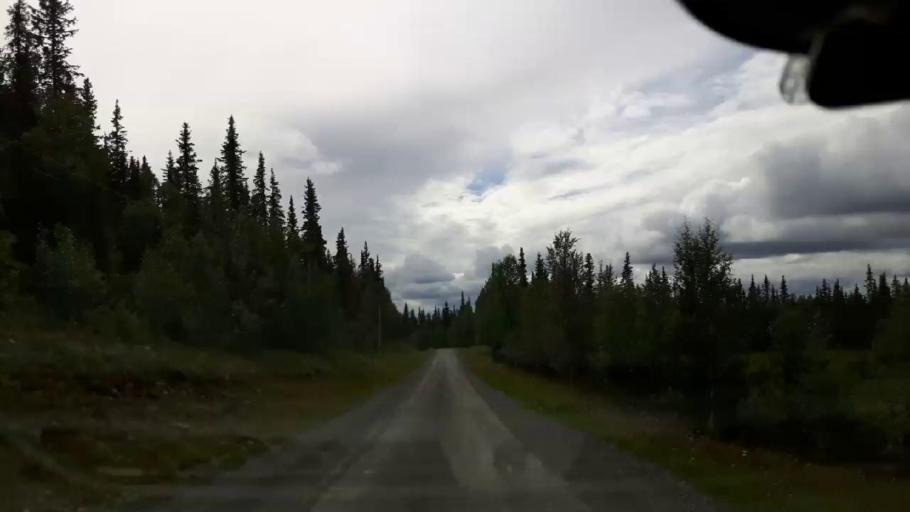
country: SE
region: Jaemtland
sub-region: Krokoms Kommun
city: Valla
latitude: 63.7550
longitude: 13.8370
